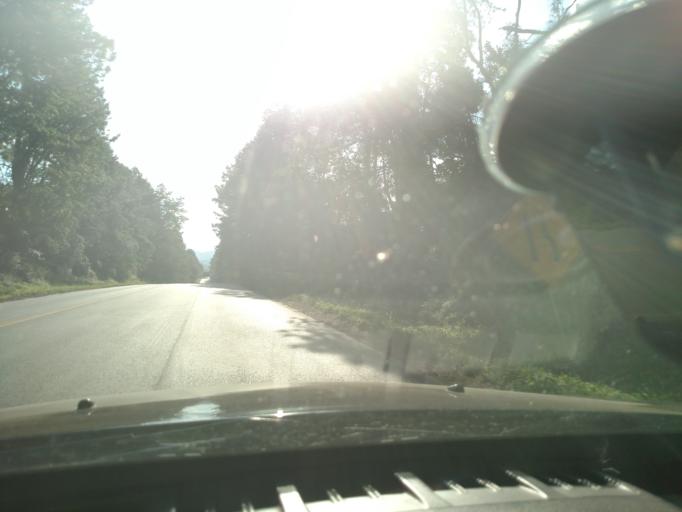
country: BR
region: Santa Catarina
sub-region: Otacilio Costa
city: Otacilio Costa
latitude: -27.3041
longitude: -50.0919
